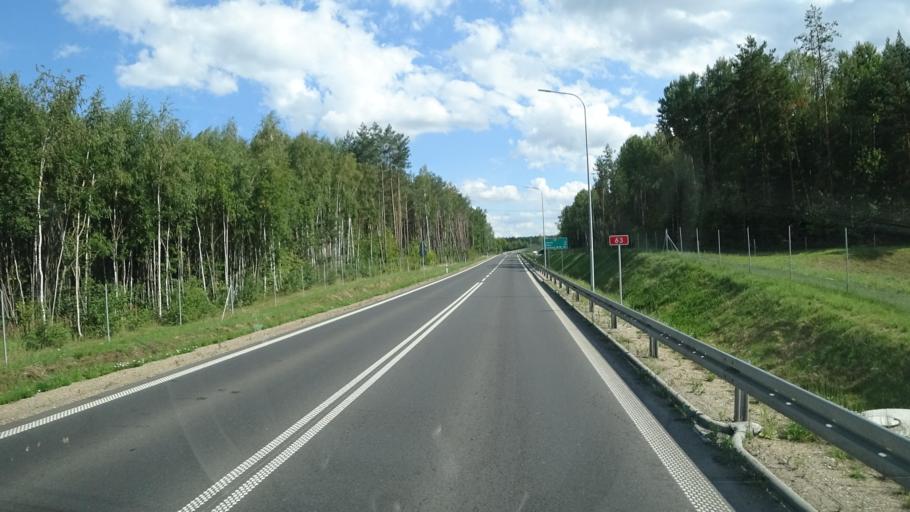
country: PL
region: Podlasie
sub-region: Powiat lomzynski
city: Piatnica
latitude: 53.0925
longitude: 22.1375
